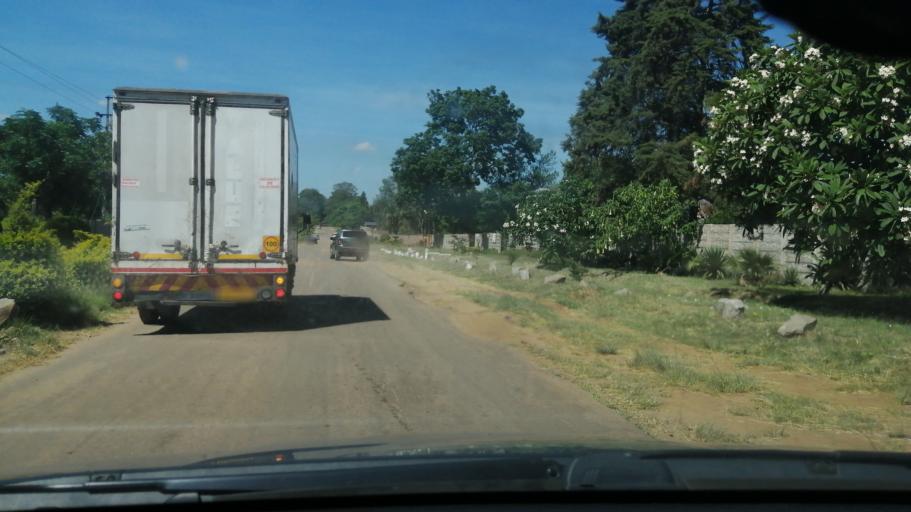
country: ZW
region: Harare
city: Epworth
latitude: -17.8201
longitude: 31.1296
